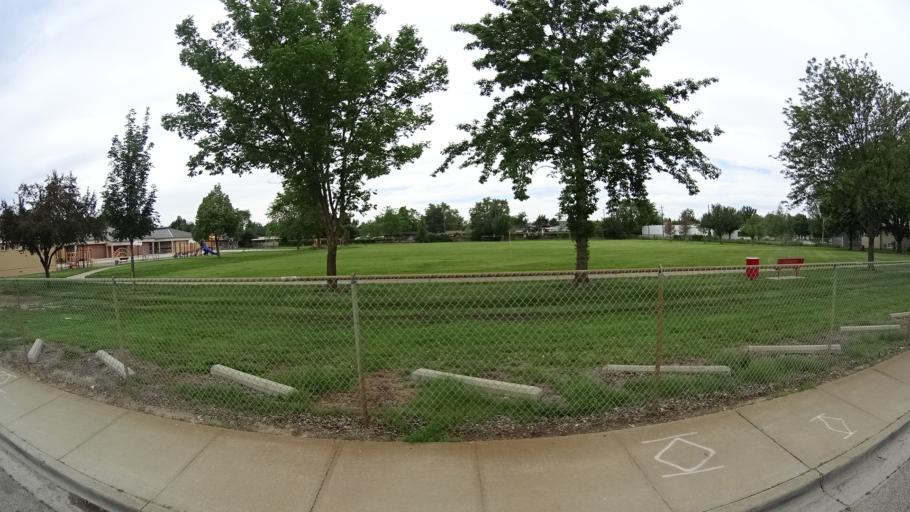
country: US
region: Idaho
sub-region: Ada County
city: Boise
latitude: 43.5825
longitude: -116.2121
